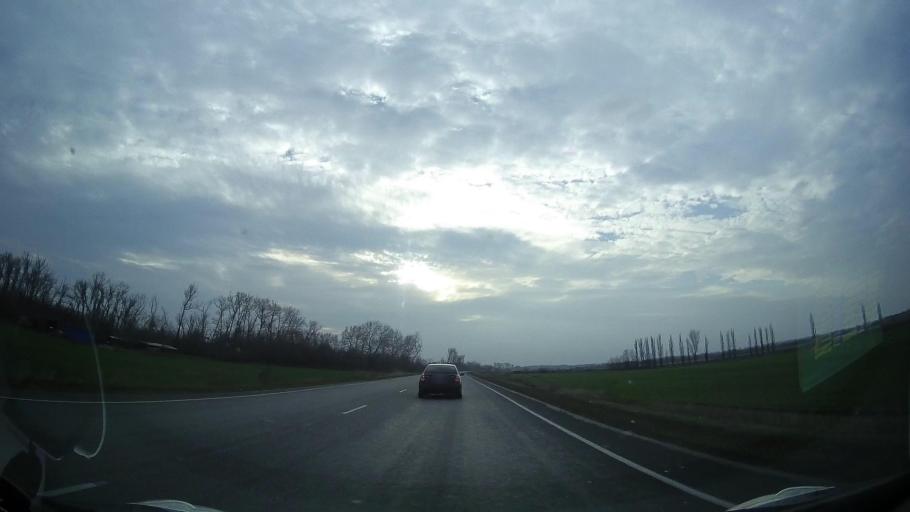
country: RU
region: Rostov
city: Ol'ginskaya
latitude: 47.1367
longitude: 39.9901
